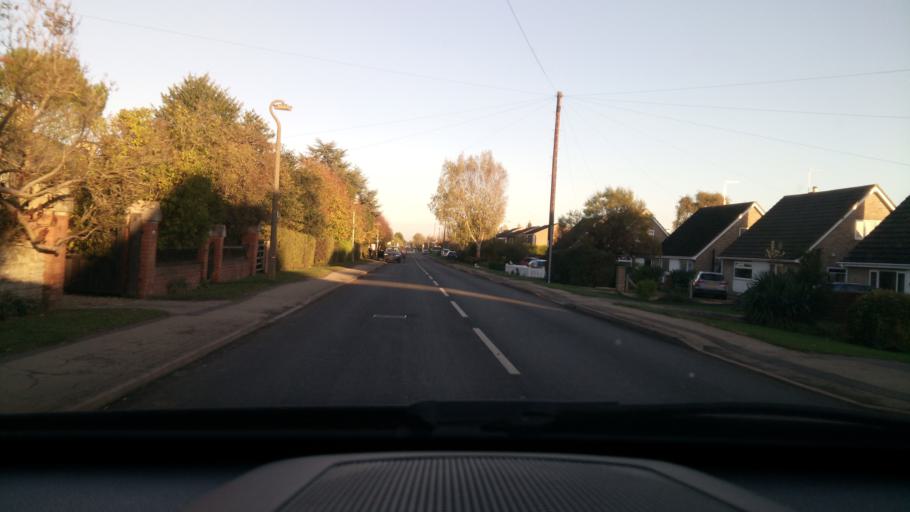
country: GB
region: England
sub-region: Peterborough
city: Helpston
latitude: 52.6355
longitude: -0.3412
